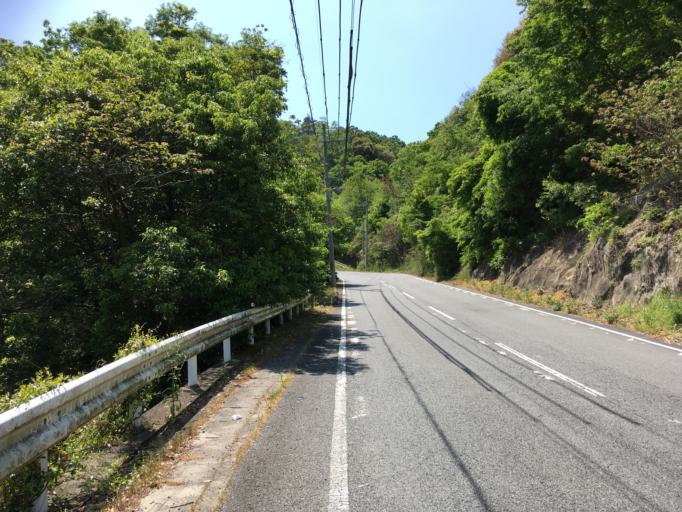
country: JP
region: Nara
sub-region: Ikoma-shi
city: Ikoma
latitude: 34.6516
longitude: 135.6866
